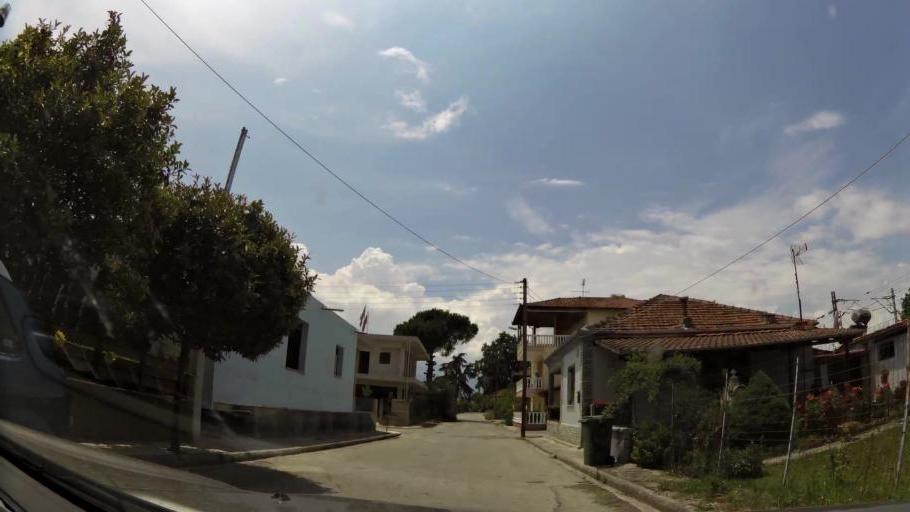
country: GR
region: Central Macedonia
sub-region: Nomos Pierias
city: Peristasi
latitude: 40.2769
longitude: 22.5401
